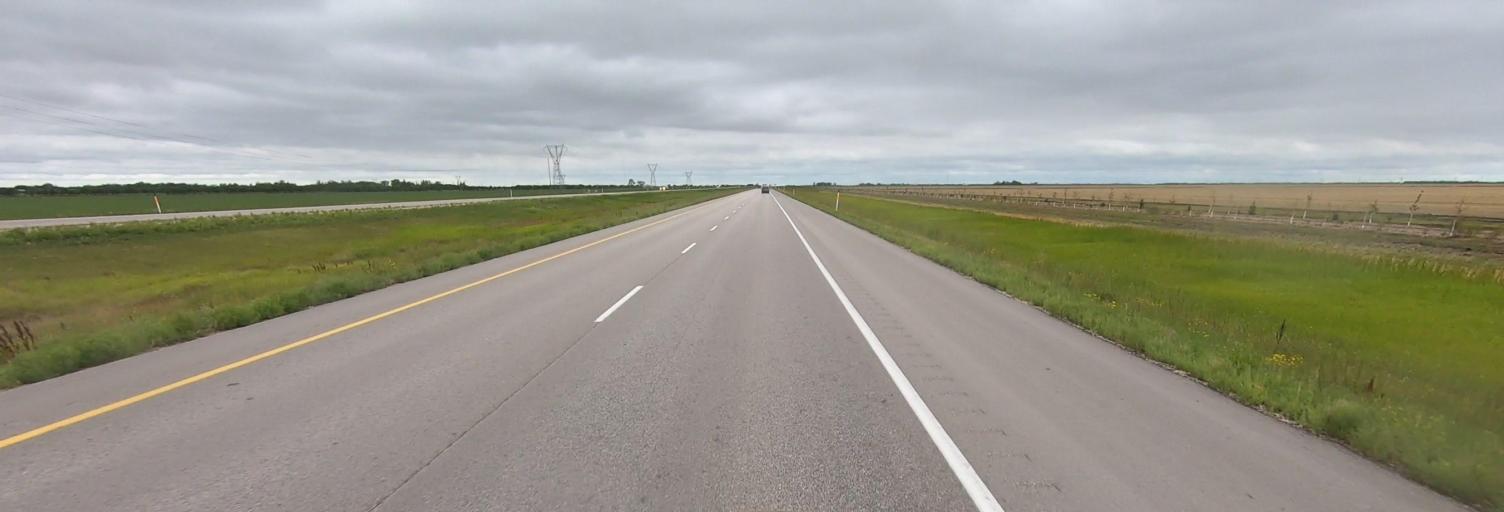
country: CA
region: Manitoba
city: Headingley
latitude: 49.8871
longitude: -97.6222
